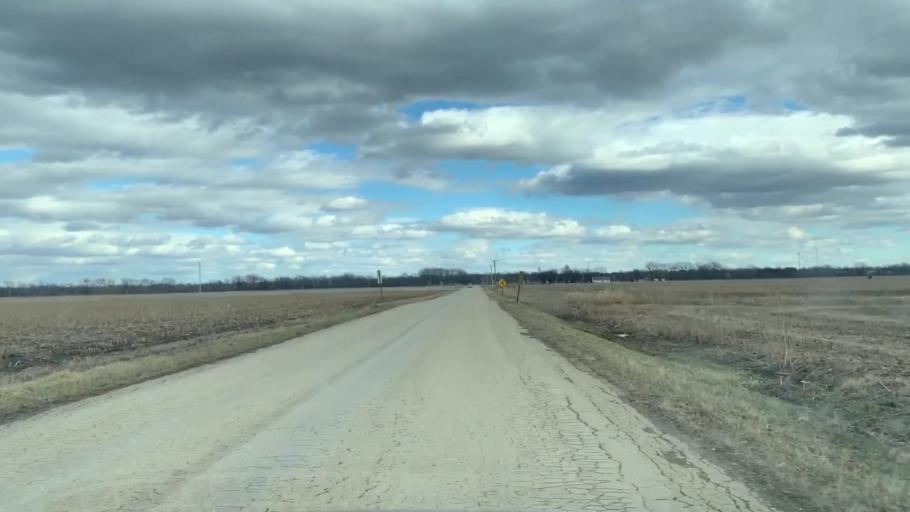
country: US
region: Kansas
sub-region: Allen County
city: Humboldt
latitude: 37.8129
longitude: -95.4643
